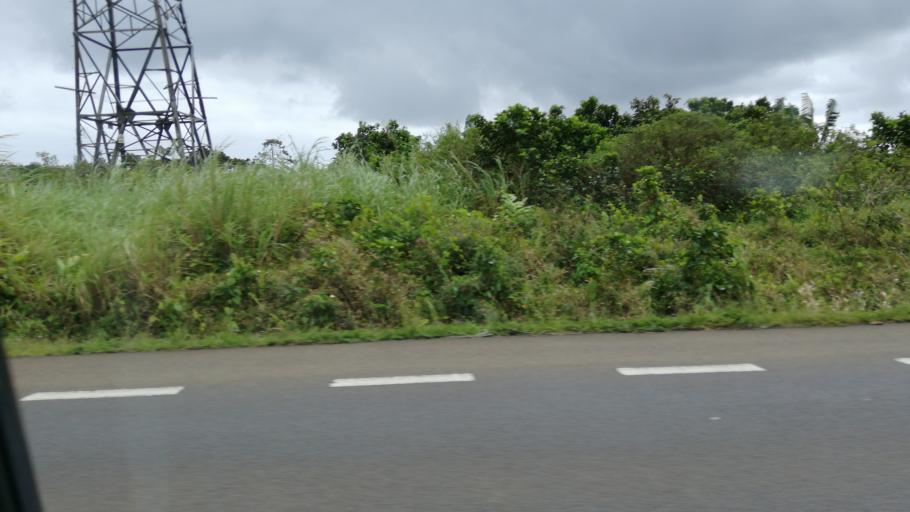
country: MU
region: Plaines Wilhems
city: Curepipe
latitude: -20.2949
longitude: 57.5431
